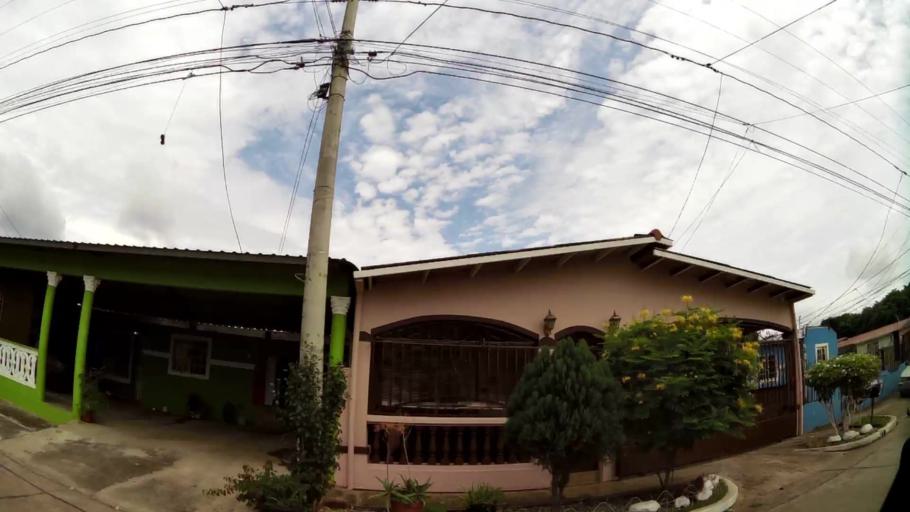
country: PA
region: Panama
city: Tocumen
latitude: 9.0407
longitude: -79.4081
